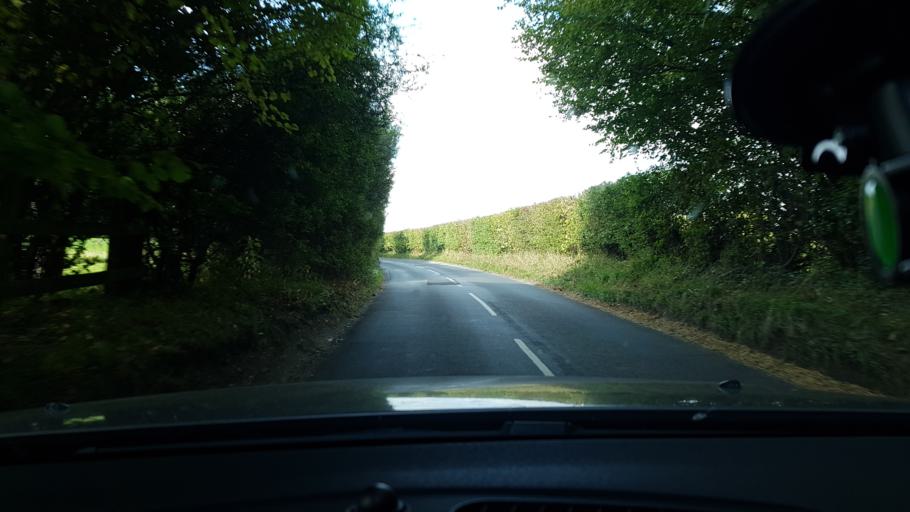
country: GB
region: England
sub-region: West Berkshire
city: Kintbury
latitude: 51.4026
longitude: -1.4696
